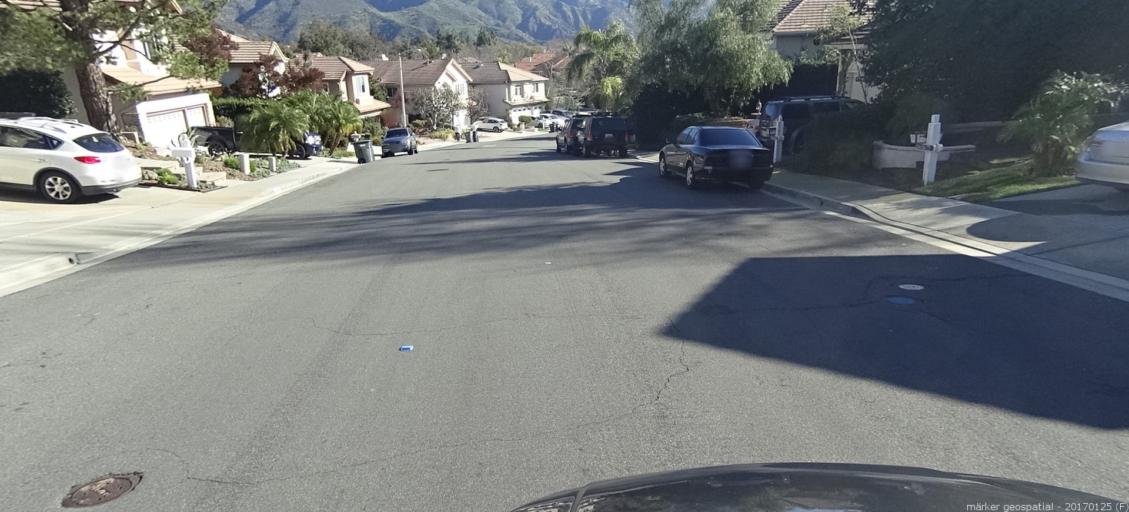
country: US
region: California
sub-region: Orange County
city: Portola Hills
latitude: 33.6859
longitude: -117.6314
